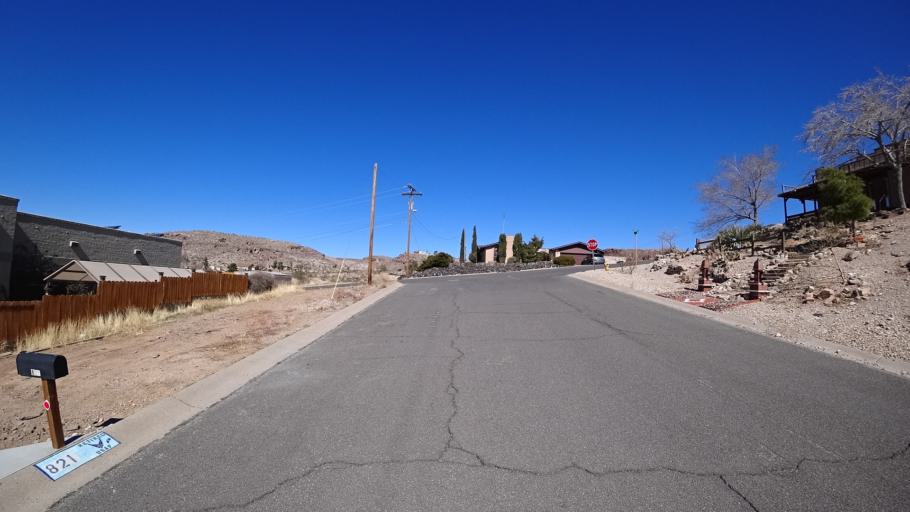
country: US
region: Arizona
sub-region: Mohave County
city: Kingman
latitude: 35.1962
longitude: -114.0588
